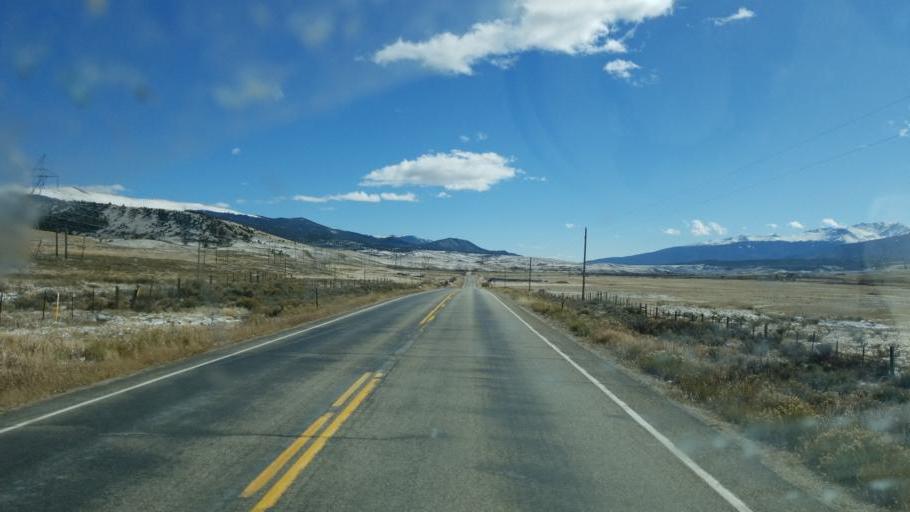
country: US
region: Colorado
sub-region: Lake County
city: Leadville
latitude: 39.1838
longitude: -106.3270
